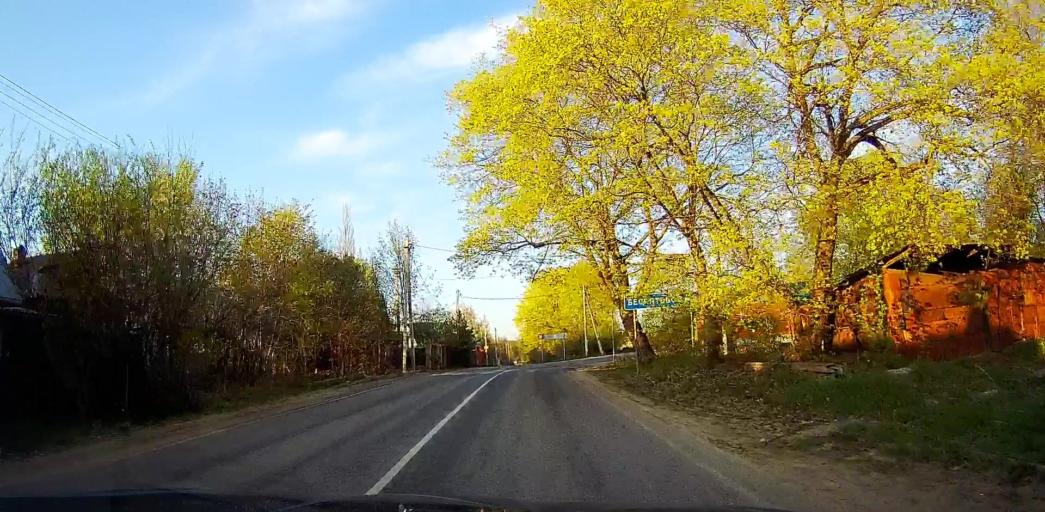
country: RU
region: Moskovskaya
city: Meshcherino
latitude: 55.2439
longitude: 38.3162
